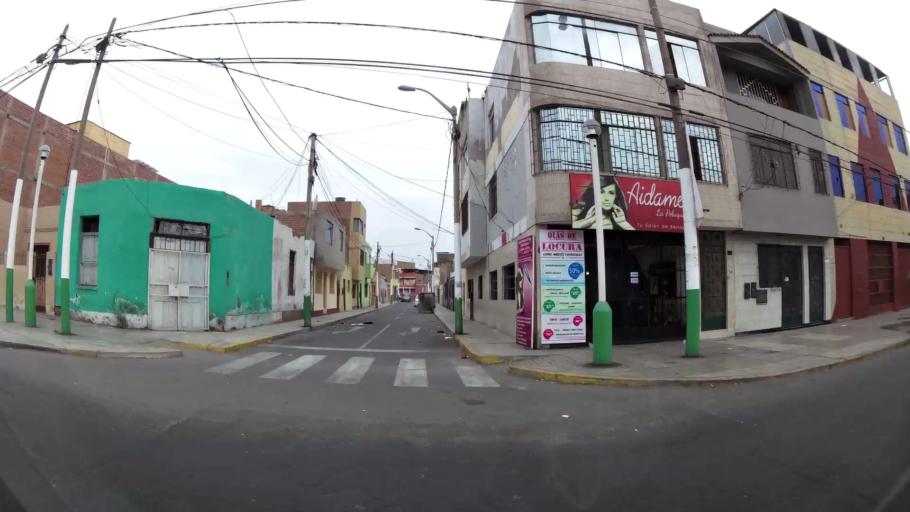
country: PE
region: Callao
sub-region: Callao
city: Callao
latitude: -12.0663
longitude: -77.1245
